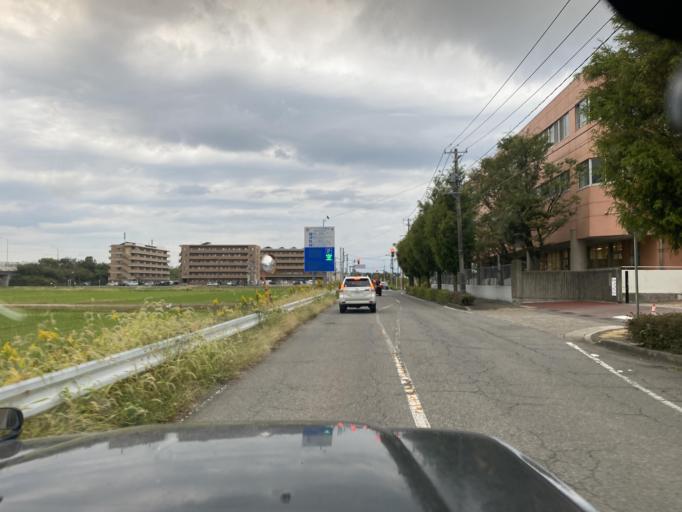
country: JP
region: Niigata
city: Niigata-shi
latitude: 37.8746
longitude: 139.0470
